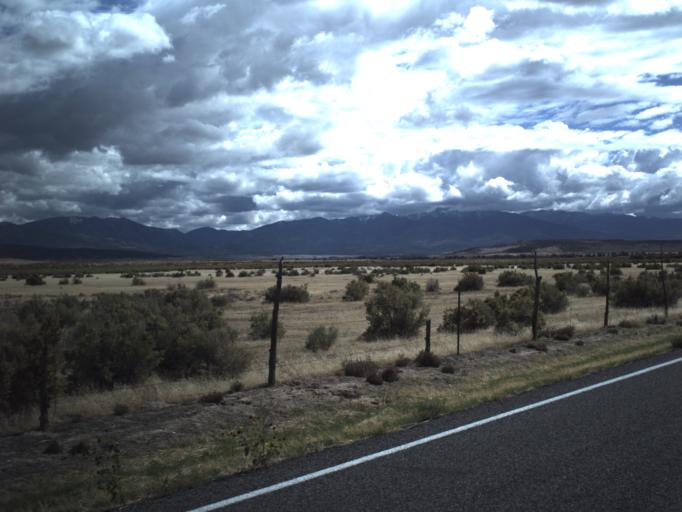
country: US
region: Utah
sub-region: Millard County
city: Fillmore
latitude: 39.0735
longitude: -112.4099
